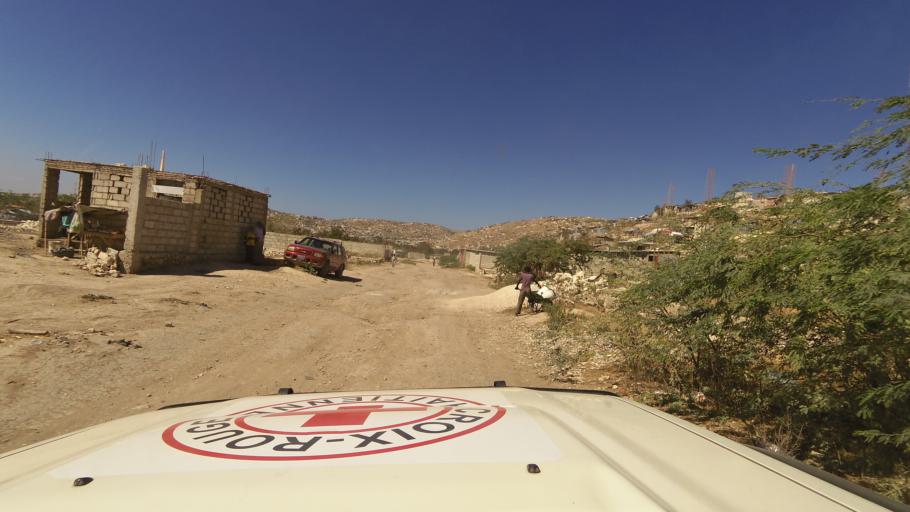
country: HT
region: Ouest
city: Croix des Bouquets
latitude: 18.6613
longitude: -72.2548
